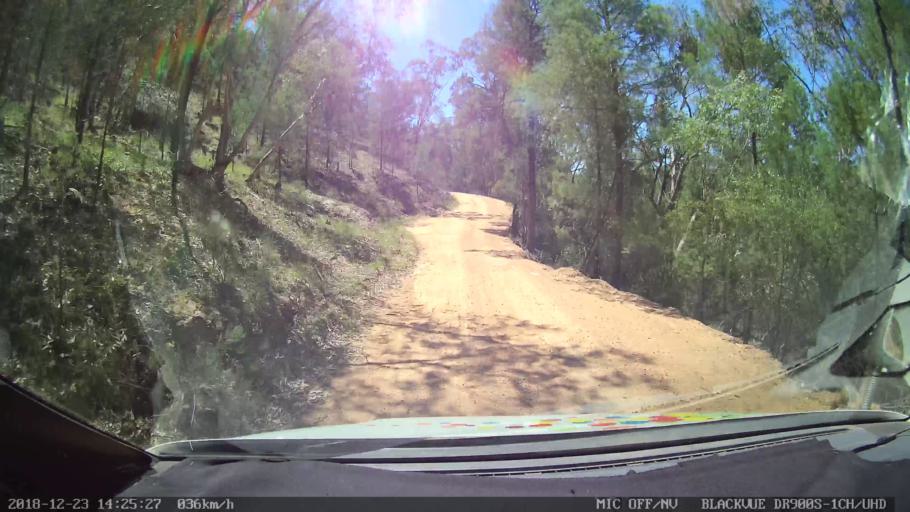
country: AU
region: New South Wales
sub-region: Tamworth Municipality
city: Manilla
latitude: -30.6268
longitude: 150.9558
